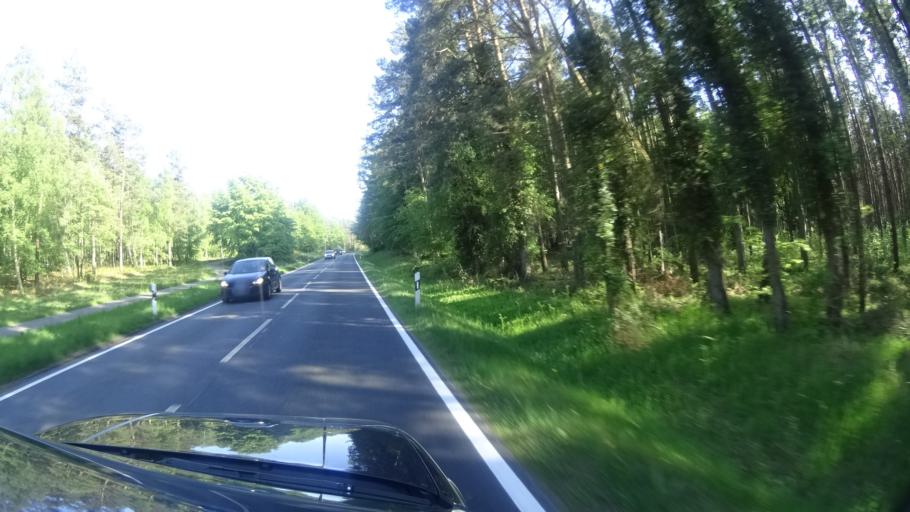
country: DE
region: Mecklenburg-Vorpommern
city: Ostseebad Prerow
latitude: 54.4217
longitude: 12.5738
